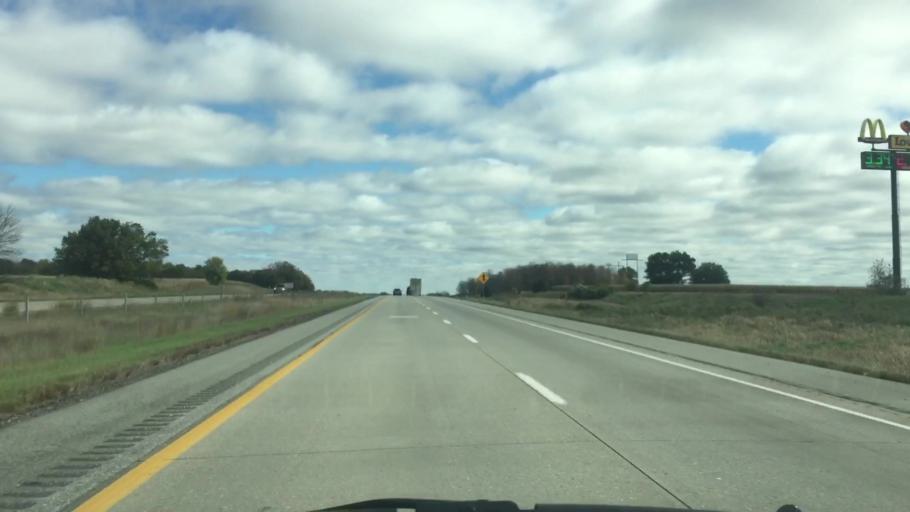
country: US
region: Iowa
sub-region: Jasper County
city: Newton
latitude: 41.6824
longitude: -92.9982
